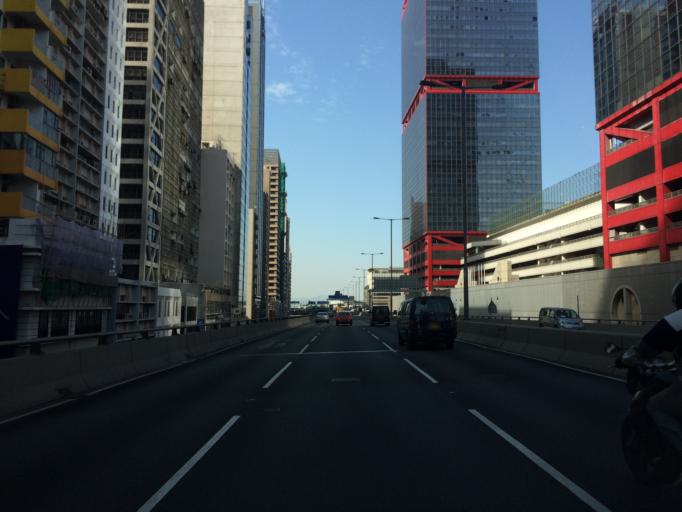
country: HK
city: Hong Kong
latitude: 22.2870
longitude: 114.1531
